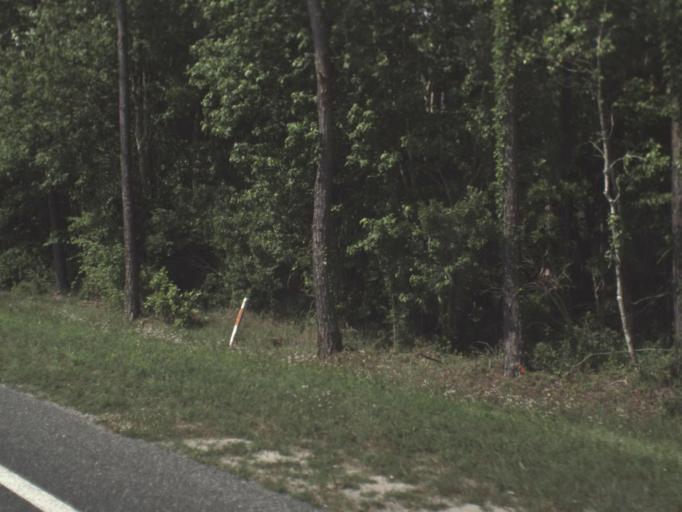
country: US
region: Florida
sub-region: Saint Johns County
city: Saint Augustine Shores
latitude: 29.7720
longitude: -81.3156
